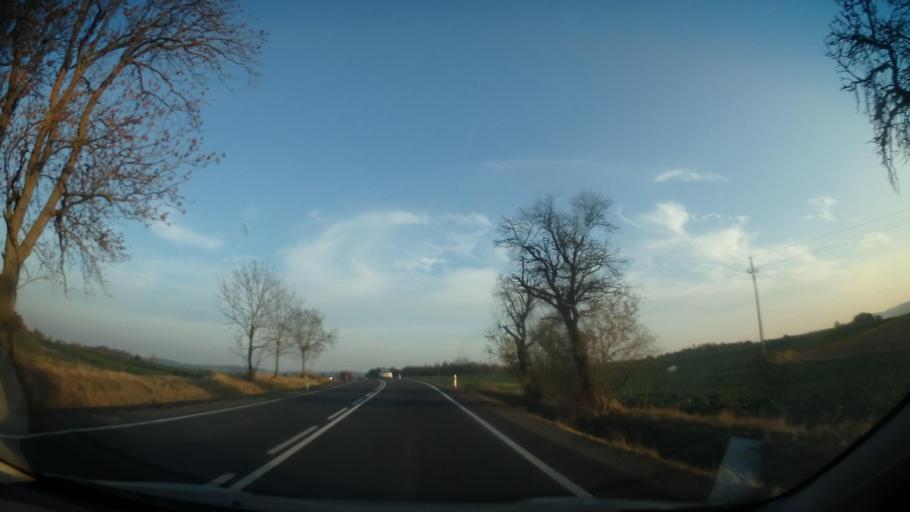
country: CZ
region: Central Bohemia
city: Postupice
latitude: 49.7439
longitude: 14.7991
